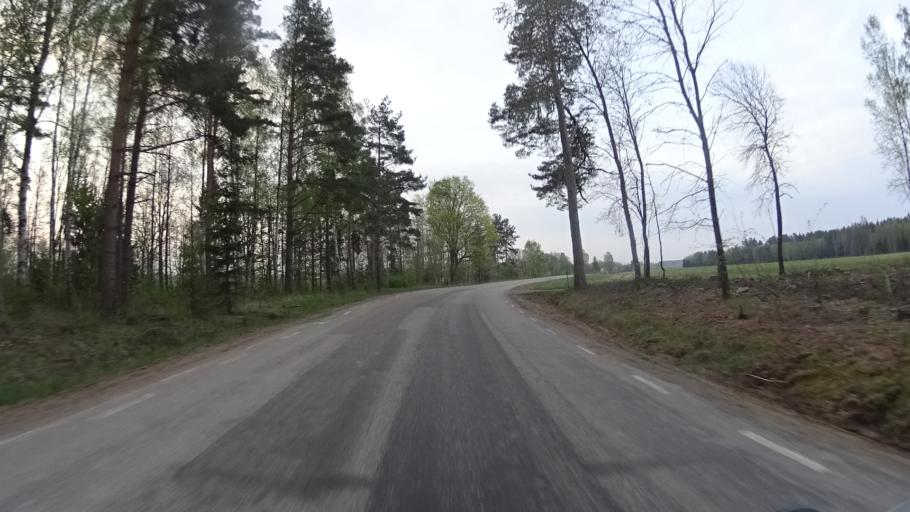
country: SE
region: Vaestra Goetaland
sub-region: Gotene Kommun
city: Kallby
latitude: 58.4848
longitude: 13.3154
